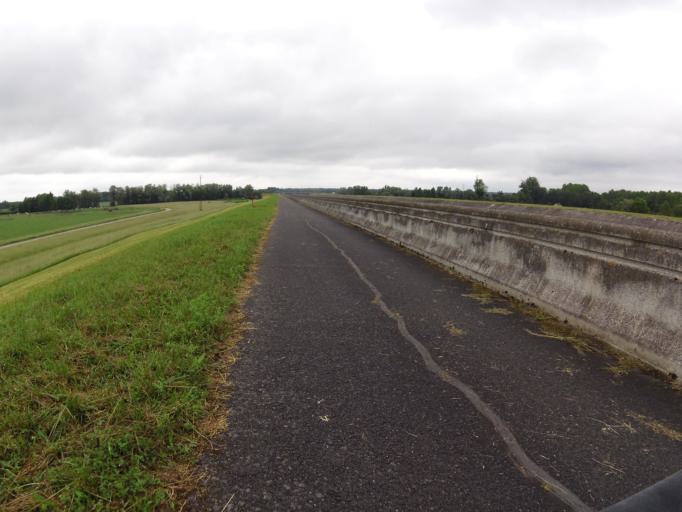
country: FR
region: Champagne-Ardenne
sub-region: Departement de la Haute-Marne
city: Villiers-en-Lieu
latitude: 48.5869
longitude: 4.8552
